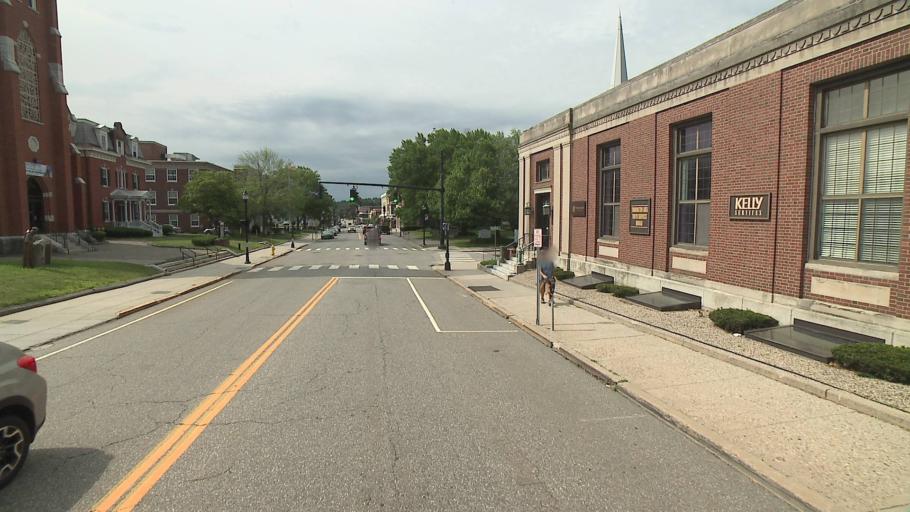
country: US
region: Connecticut
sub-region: Litchfield County
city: Torrington
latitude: 41.8041
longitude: -73.1214
